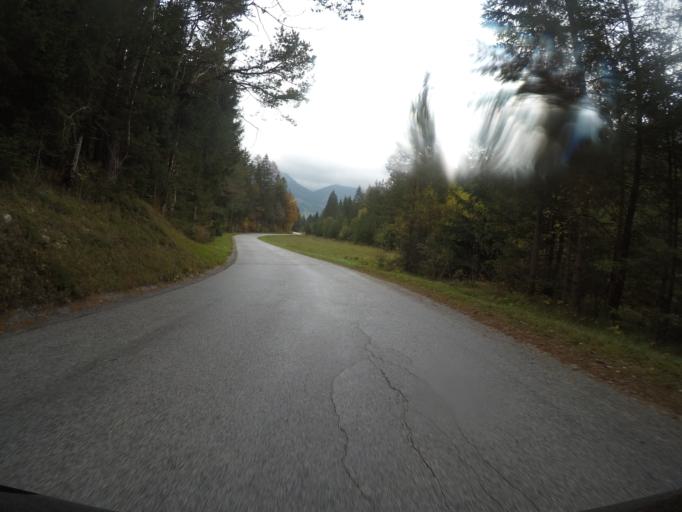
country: SI
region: Kranjska Gora
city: Mojstrana
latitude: 46.4520
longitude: 13.9283
